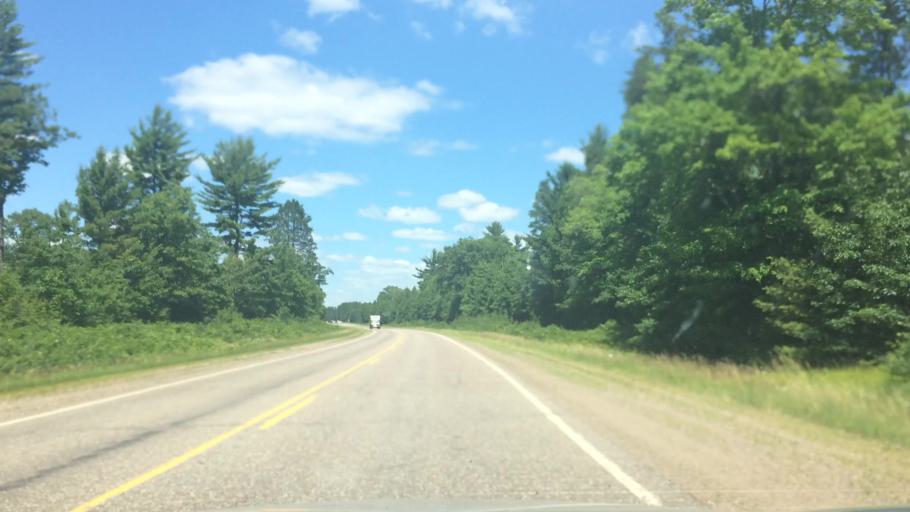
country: US
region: Wisconsin
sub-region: Vilas County
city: Lac du Flambeau
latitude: 46.0744
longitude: -89.6440
